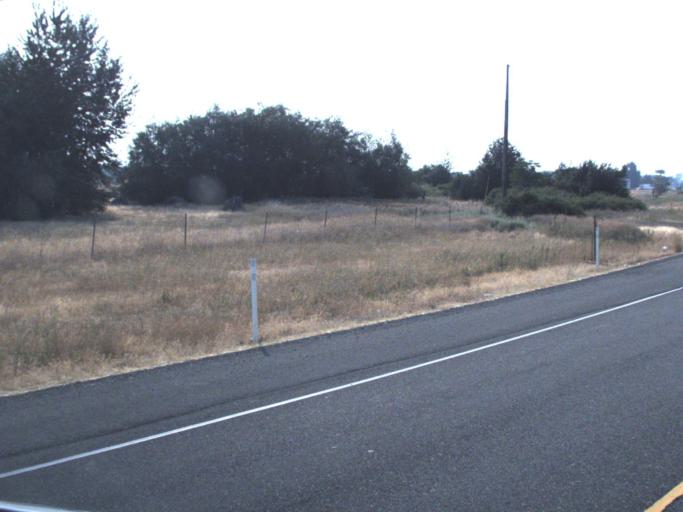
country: US
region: Washington
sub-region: Kittitas County
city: Ellensburg
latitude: 47.0122
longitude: -120.5936
